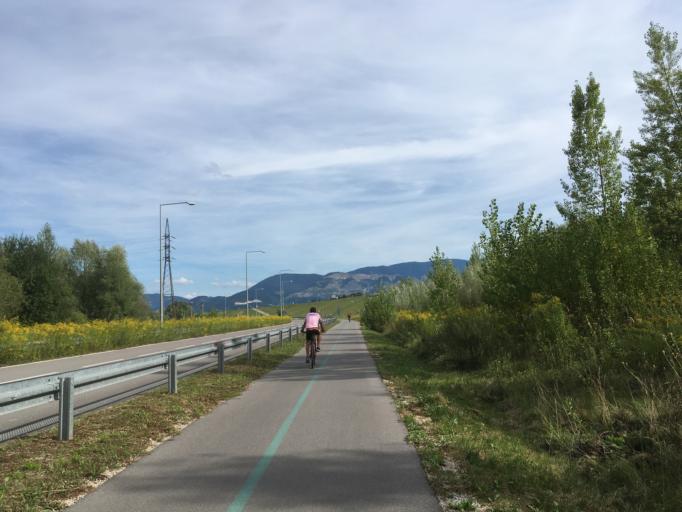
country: SK
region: Zilinsky
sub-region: Okres Zilina
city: Zilina
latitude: 49.2183
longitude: 18.7767
